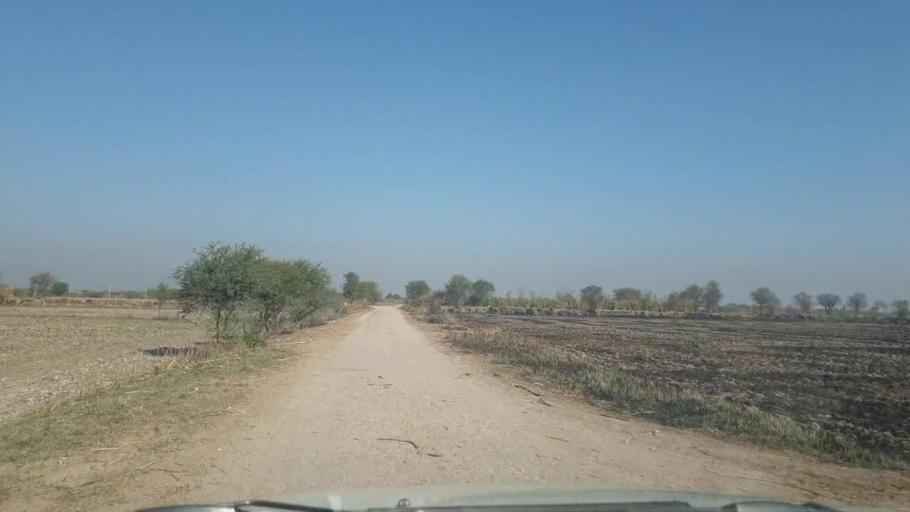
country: PK
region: Sindh
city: Mirpur Khas
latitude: 25.5113
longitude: 69.1497
